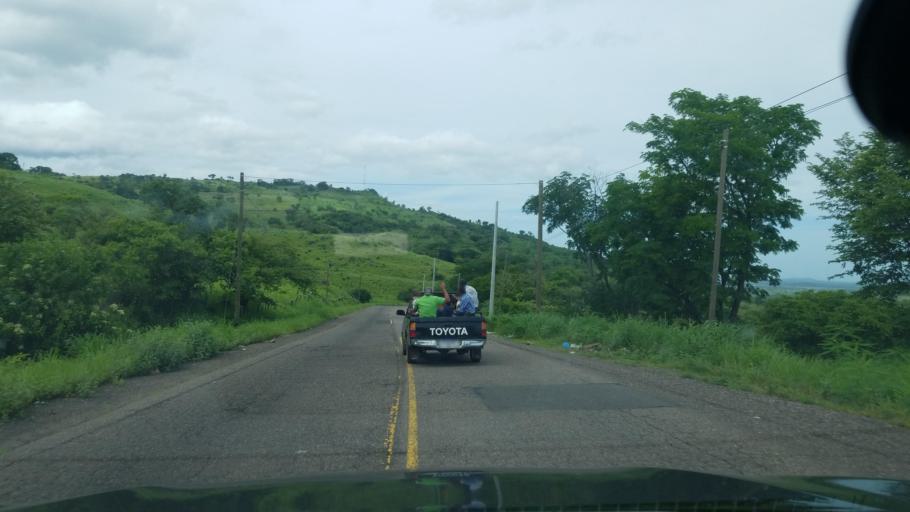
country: HN
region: Choluteca
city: Corpus
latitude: 13.3767
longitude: -87.0581
